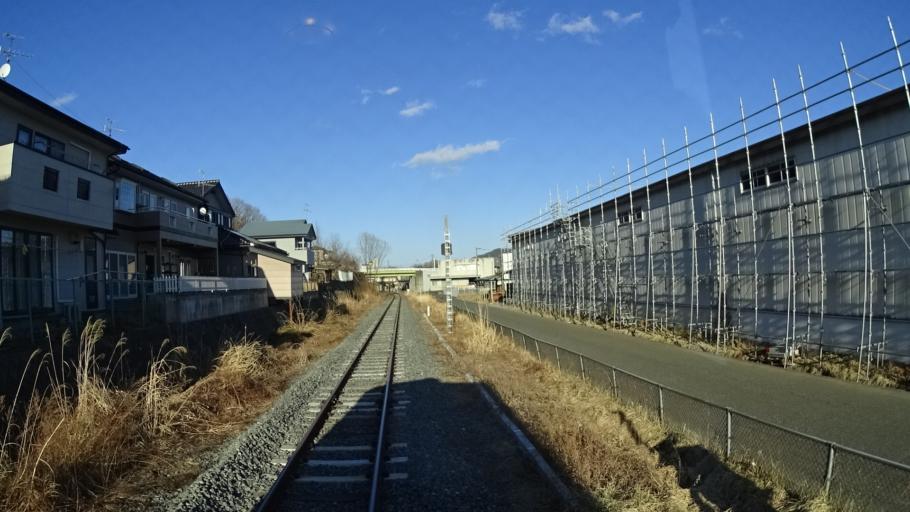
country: JP
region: Iwate
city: Miyako
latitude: 39.6258
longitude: 141.9566
